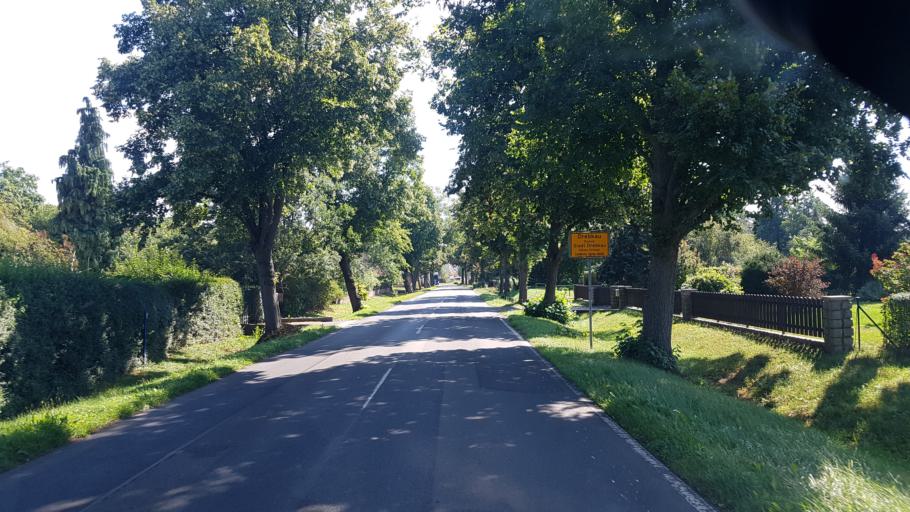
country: DE
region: Brandenburg
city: Drebkau
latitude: 51.6600
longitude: 14.2112
